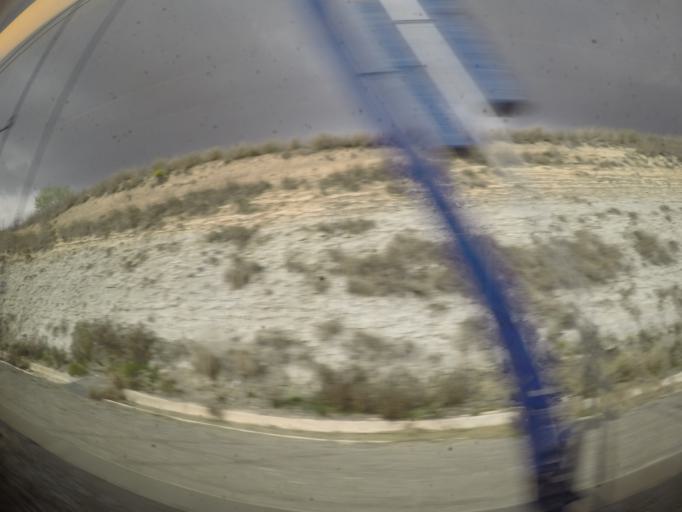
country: ES
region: Catalonia
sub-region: Provincia de Barcelona
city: Castellet
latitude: 41.3074
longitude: 1.6476
